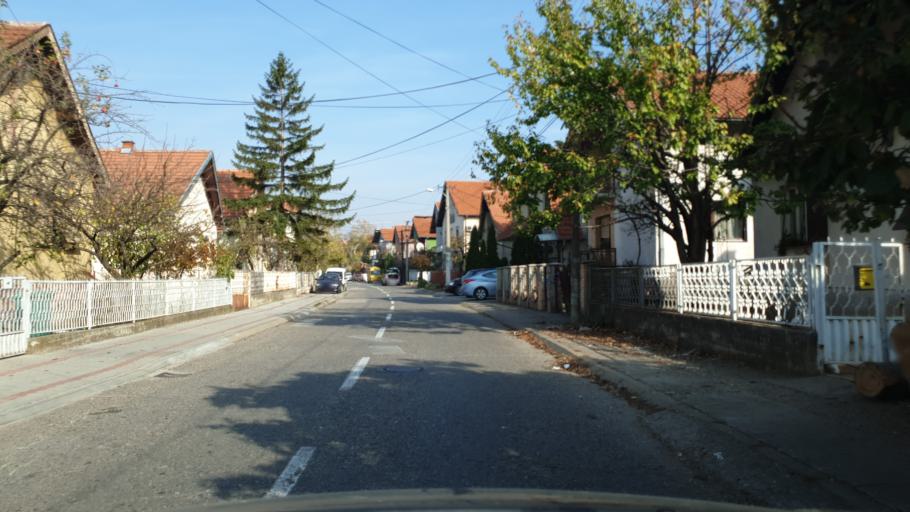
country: RS
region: Central Serbia
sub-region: Pomoravski Okrug
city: Paracin
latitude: 43.8554
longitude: 21.4243
